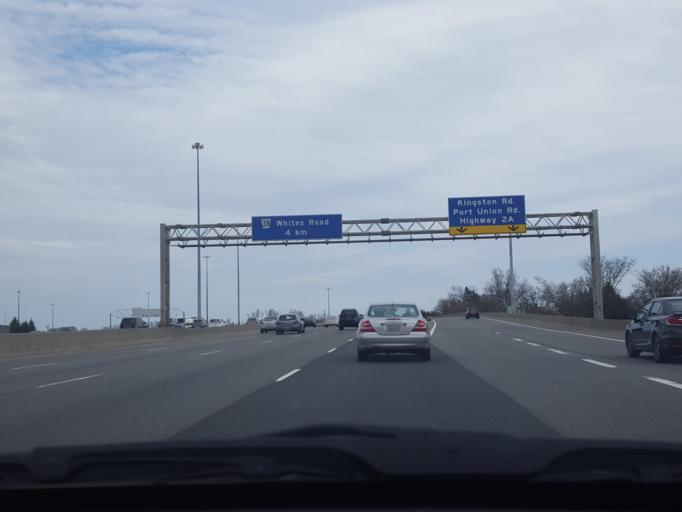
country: CA
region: Ontario
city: Scarborough
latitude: 43.7966
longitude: -79.1587
